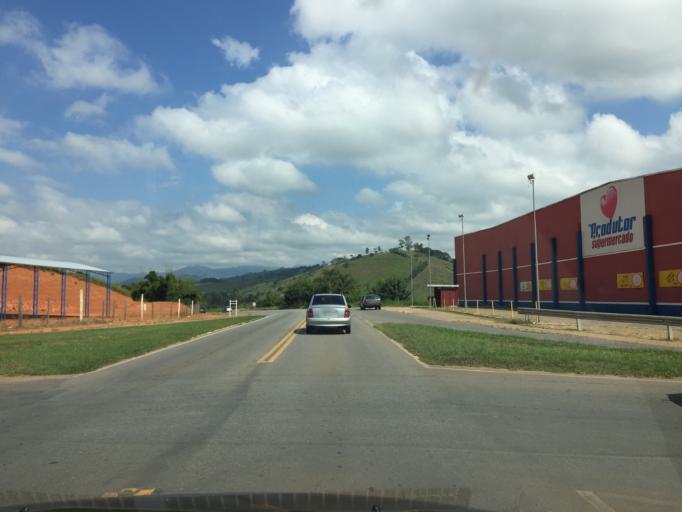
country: BR
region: Minas Gerais
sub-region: Itanhandu
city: Itanhandu
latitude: -22.3052
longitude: -44.9300
